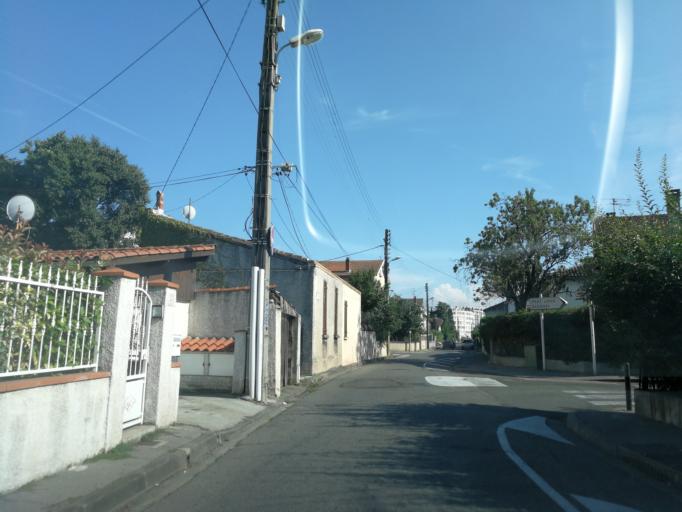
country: FR
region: Midi-Pyrenees
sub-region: Departement de la Haute-Garonne
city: Toulouse
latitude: 43.6266
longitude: 1.4263
